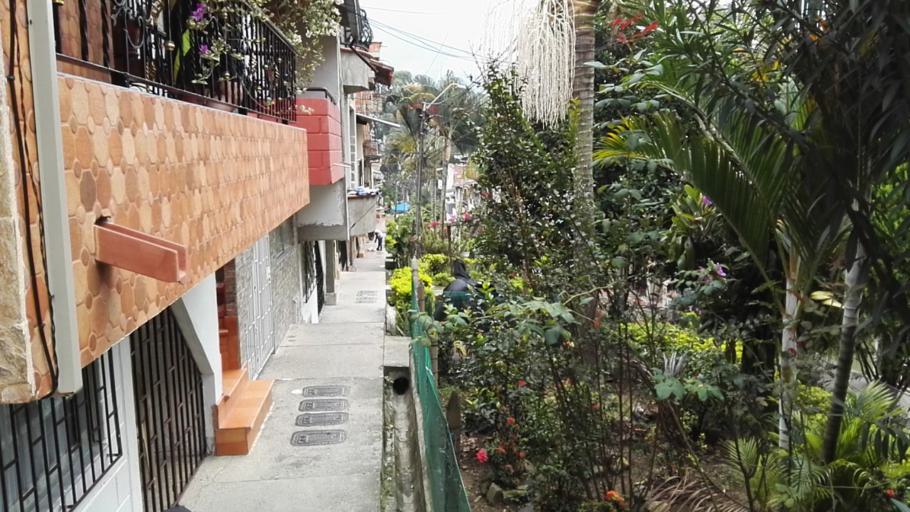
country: CO
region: Antioquia
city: Municipio de Copacabana
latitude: 6.3460
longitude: -75.5314
